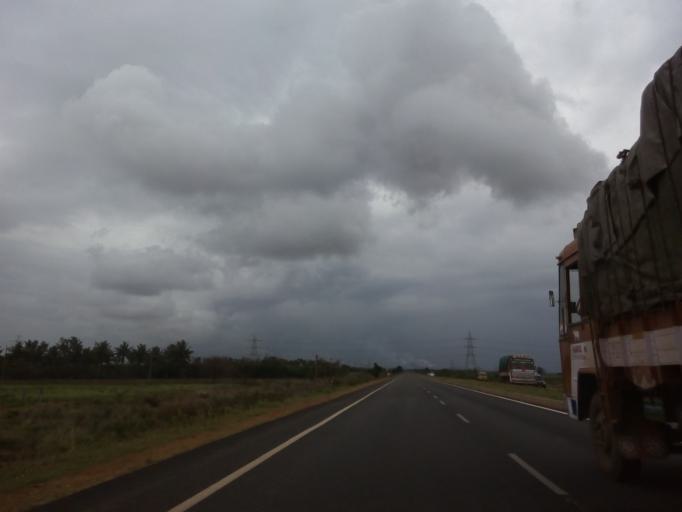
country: IN
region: Karnataka
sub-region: Davanagere
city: Harihar
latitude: 14.5450
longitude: 75.7484
